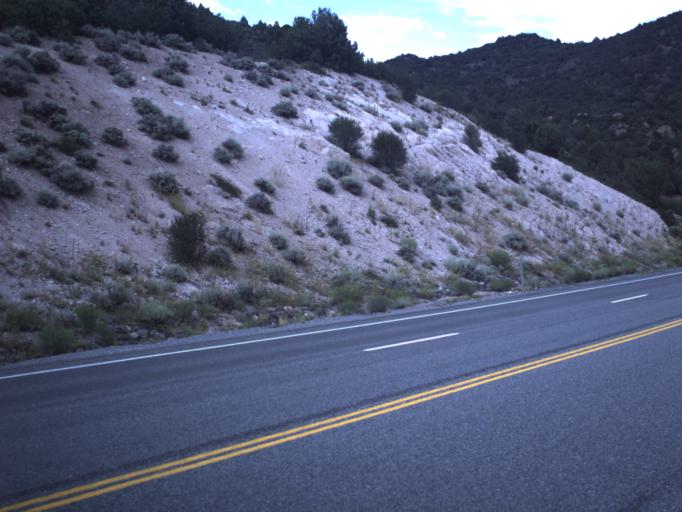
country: US
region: Utah
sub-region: Garfield County
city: Panguitch
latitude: 38.0252
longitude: -112.5268
